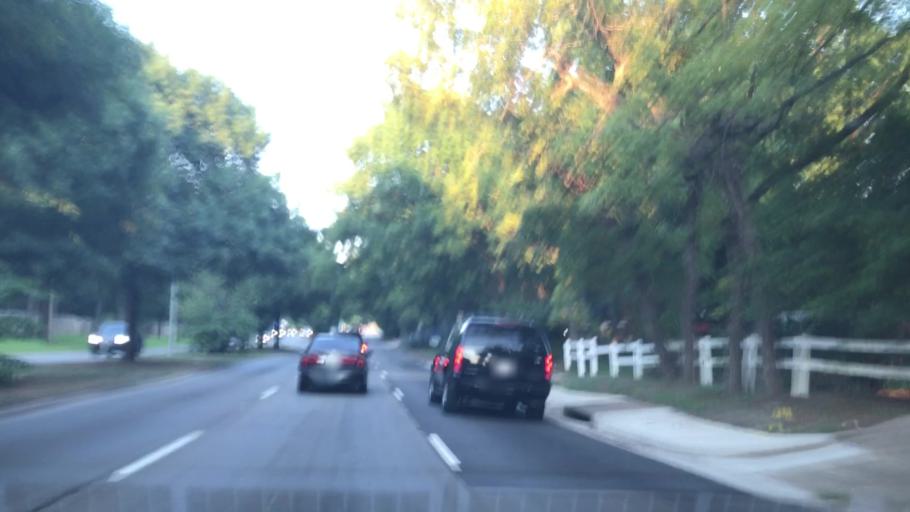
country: US
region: Texas
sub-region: Dallas County
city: University Park
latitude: 32.9097
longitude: -96.7834
